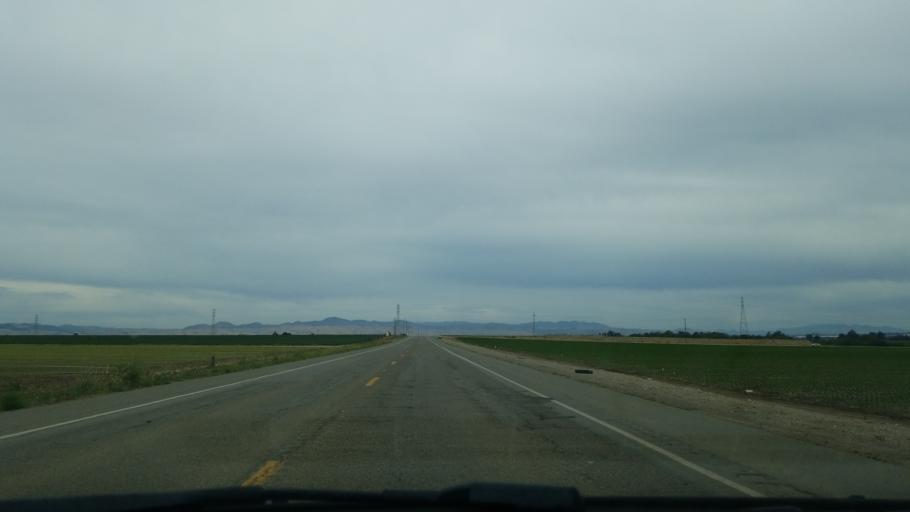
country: US
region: California
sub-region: Santa Barbara County
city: Guadalupe
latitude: 34.9188
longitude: -120.5103
